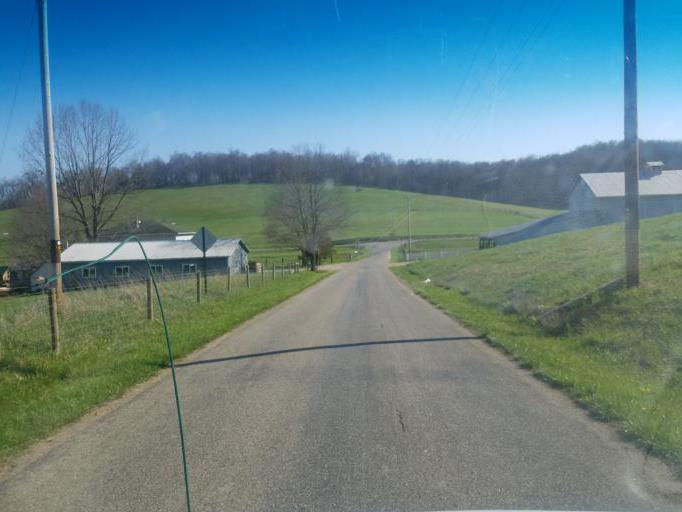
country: US
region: Ohio
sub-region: Knox County
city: Oak Hill
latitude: 40.2590
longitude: -82.2227
